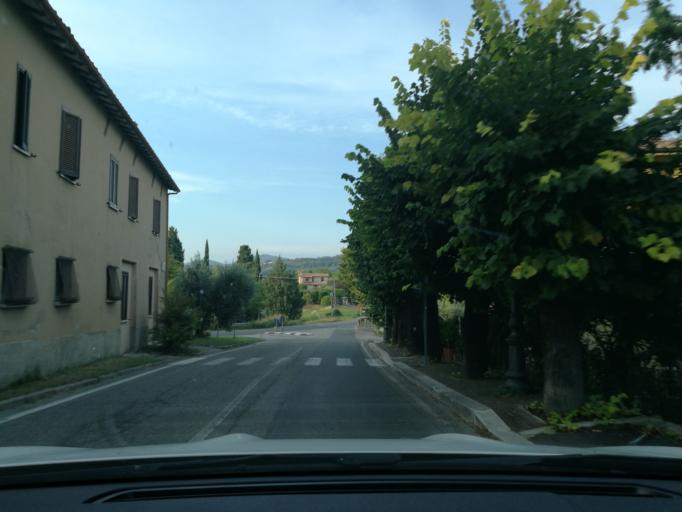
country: IT
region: Umbria
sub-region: Provincia di Terni
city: San Gemini
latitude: 42.6166
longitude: 12.5491
